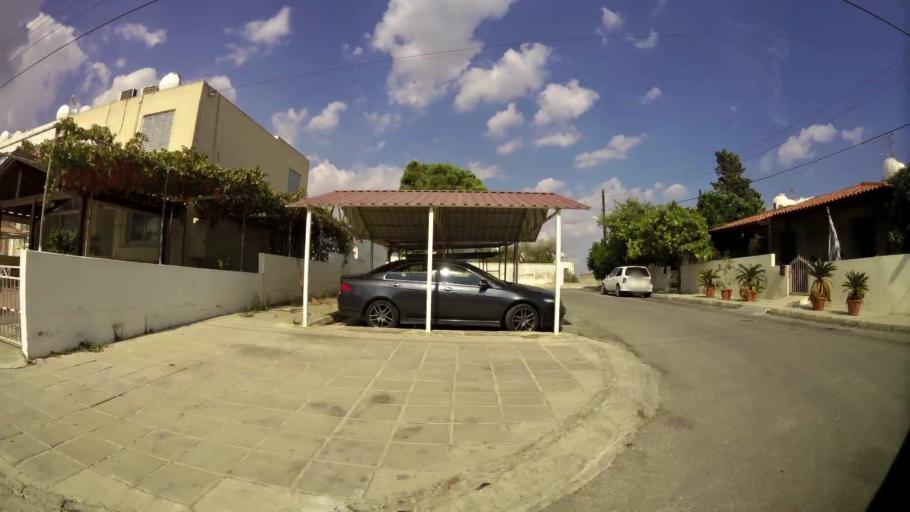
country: CY
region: Larnaka
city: Larnaca
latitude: 34.9076
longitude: 33.5972
